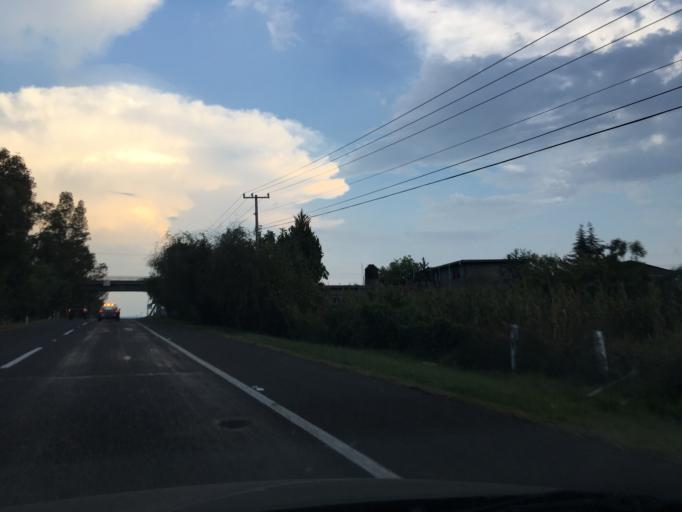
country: MX
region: Michoacan
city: Lagunillas
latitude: 19.5560
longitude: -101.3914
